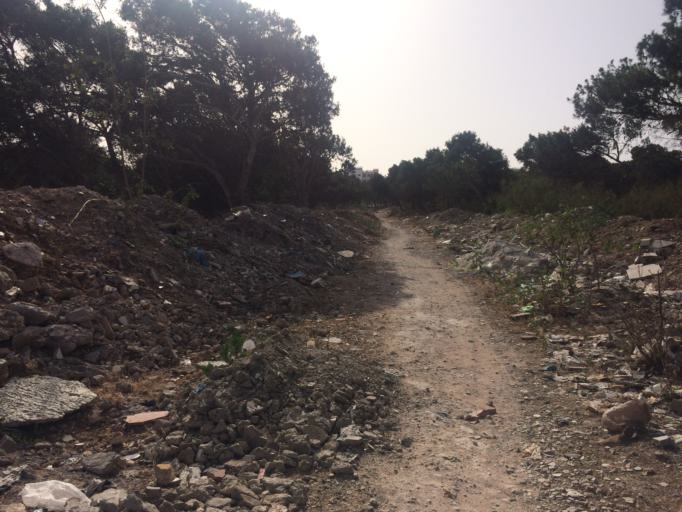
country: MA
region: Doukkala-Abda
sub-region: Safi
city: Safi
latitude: 32.3183
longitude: -9.2328
